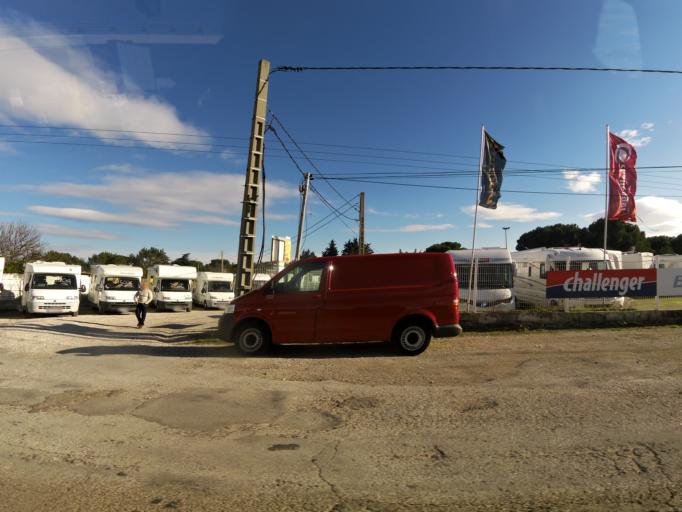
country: FR
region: Languedoc-Roussillon
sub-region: Departement du Gard
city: Milhaud
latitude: 43.8024
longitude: 4.3194
